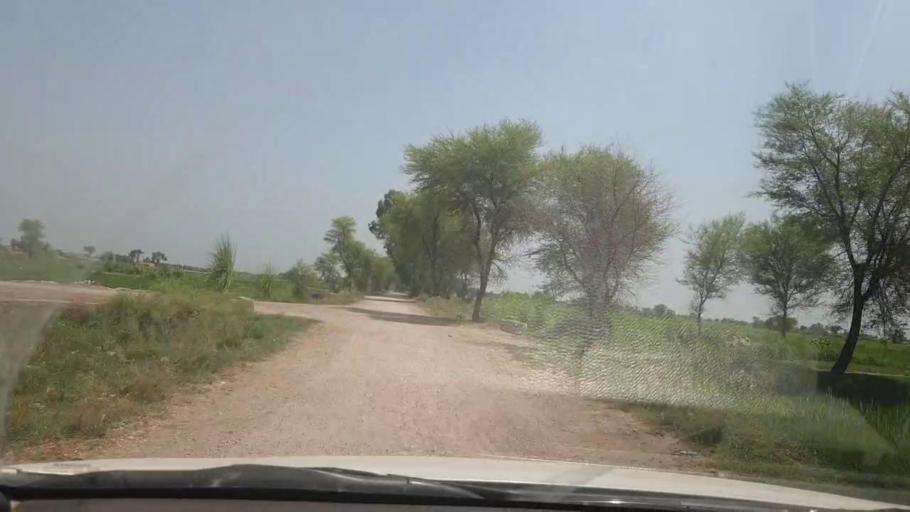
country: PK
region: Sindh
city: Lakhi
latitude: 27.8835
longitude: 68.7421
